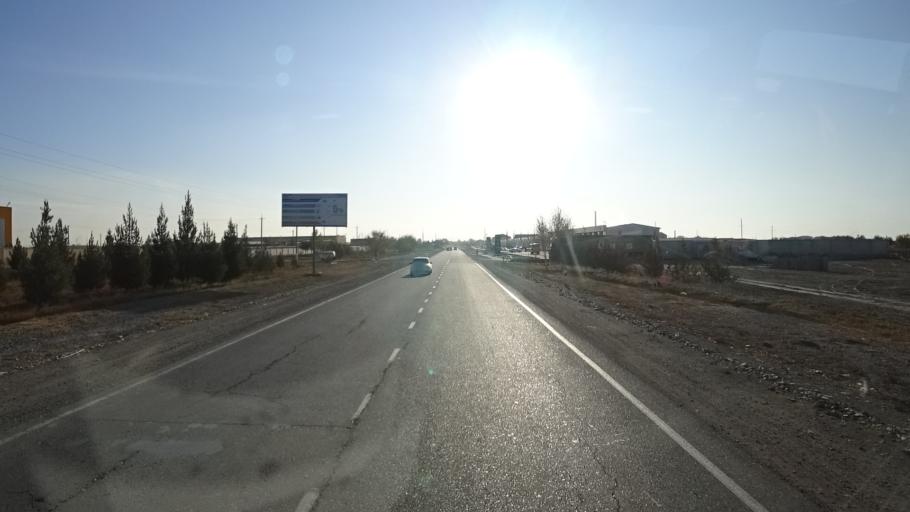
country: UZ
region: Navoiy
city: Beshrabot
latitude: 40.1706
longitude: 65.3375
